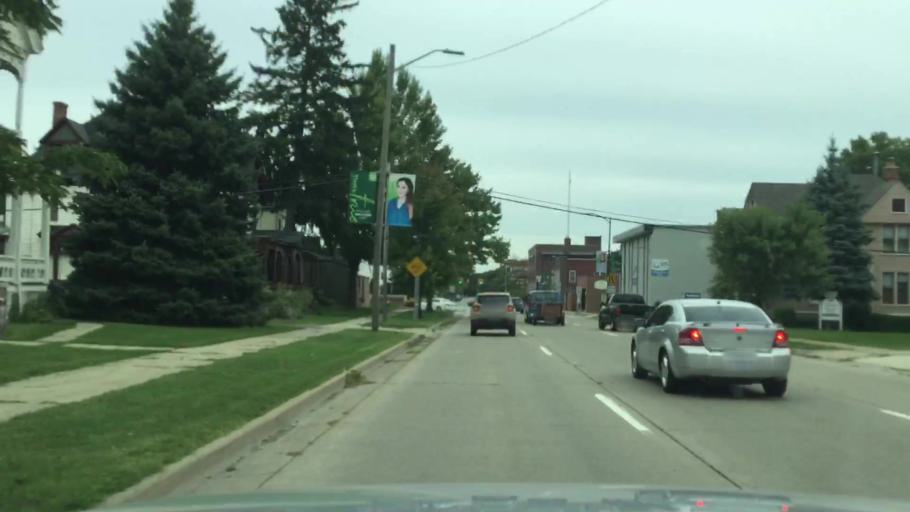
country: US
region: Michigan
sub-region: Washtenaw County
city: Ypsilanti
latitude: 42.2390
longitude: -83.6131
